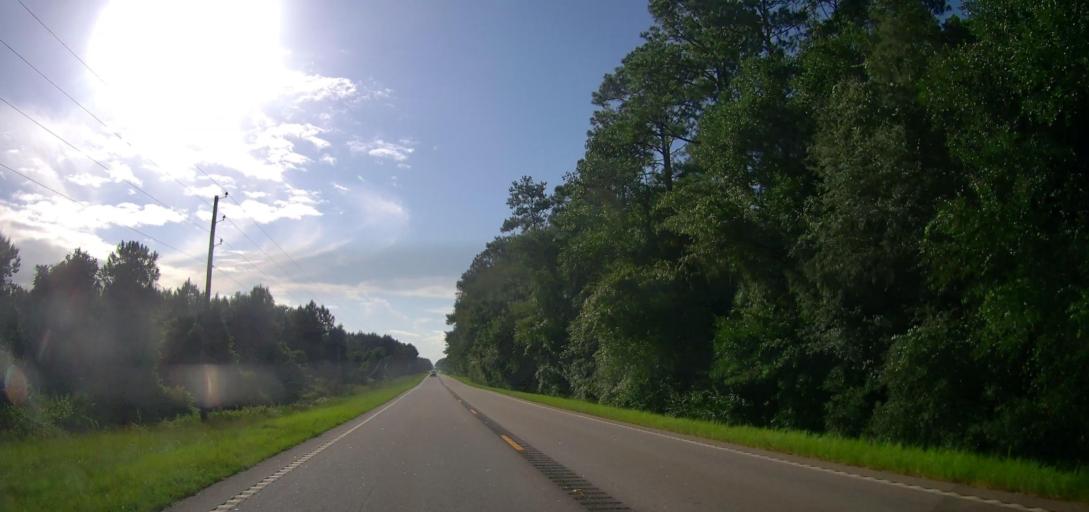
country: US
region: Georgia
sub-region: Coffee County
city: Douglas
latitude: 31.4648
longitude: -82.7576
